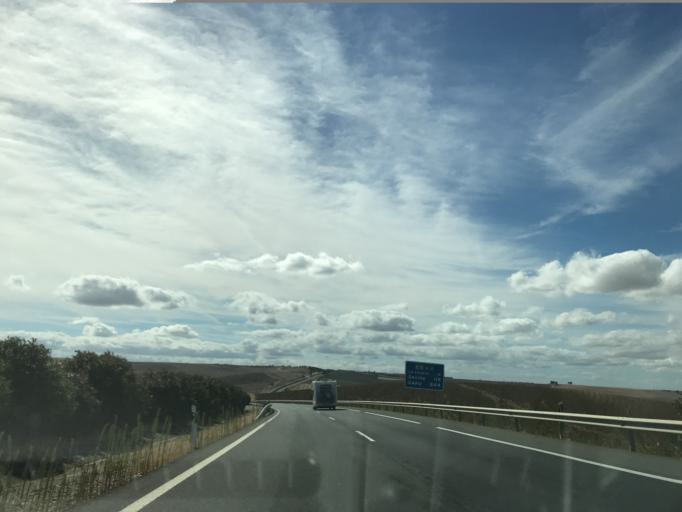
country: ES
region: Andalusia
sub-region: Province of Cordoba
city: La Victoria
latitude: 37.7442
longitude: -4.8487
